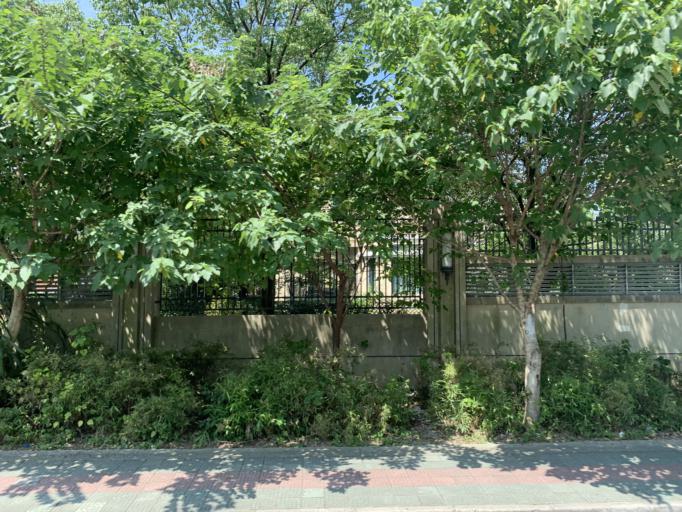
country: CN
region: Shanghai Shi
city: Huamu
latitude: 31.1777
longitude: 121.5343
